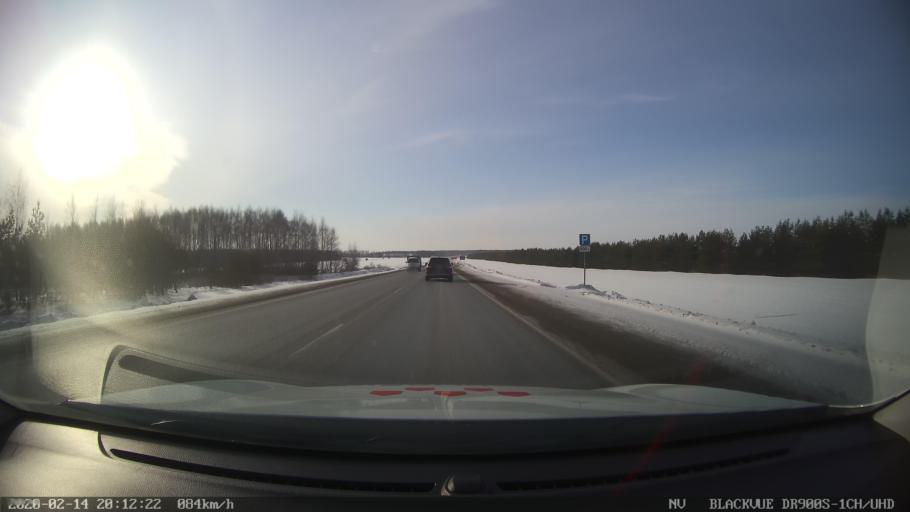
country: RU
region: Tatarstan
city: Verkhniy Uslon
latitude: 55.6666
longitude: 48.8635
